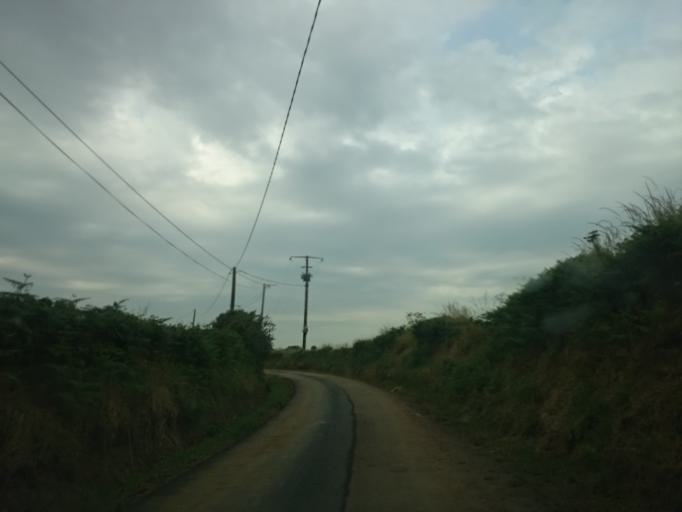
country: FR
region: Brittany
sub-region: Departement du Finistere
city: Le Conquet
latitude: 48.3981
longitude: -4.7665
